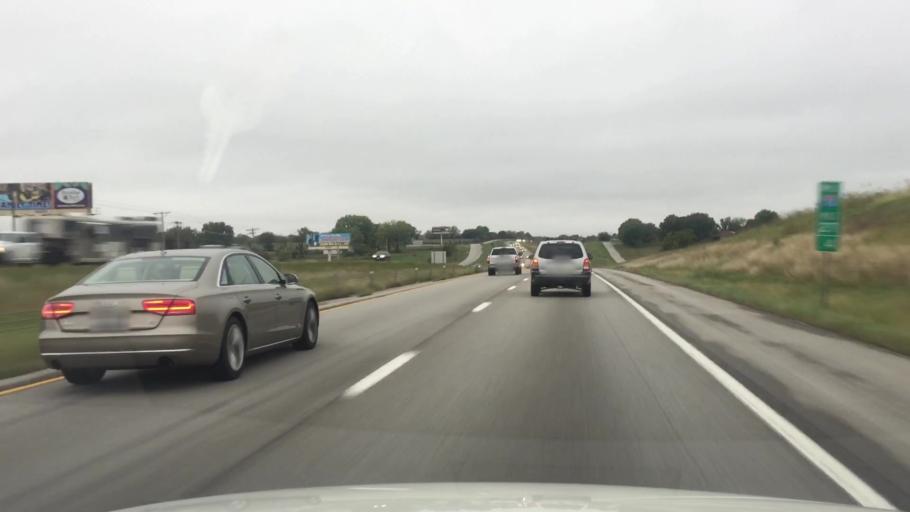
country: US
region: Missouri
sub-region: Jackson County
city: Oak Grove
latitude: 39.0168
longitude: -94.1437
